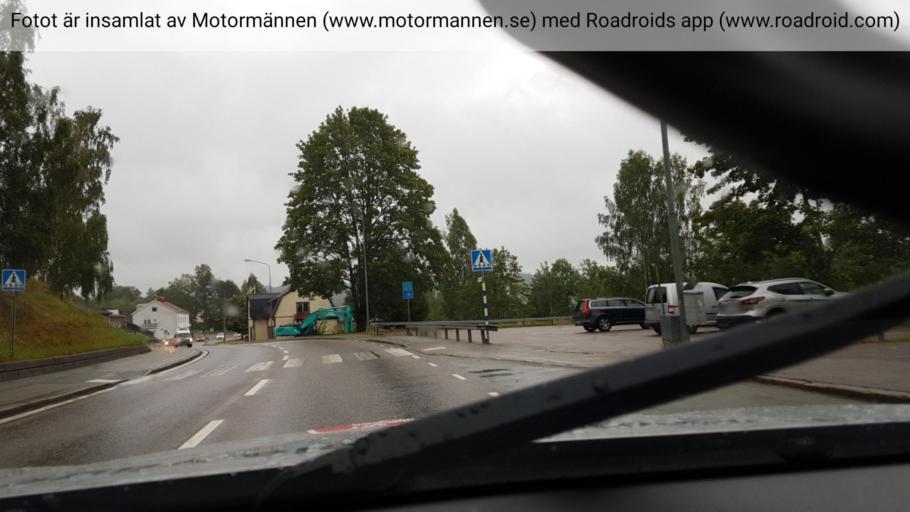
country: SE
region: Vaestra Goetaland
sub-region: Bengtsfors Kommun
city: Billingsfors
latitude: 58.9820
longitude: 12.2490
